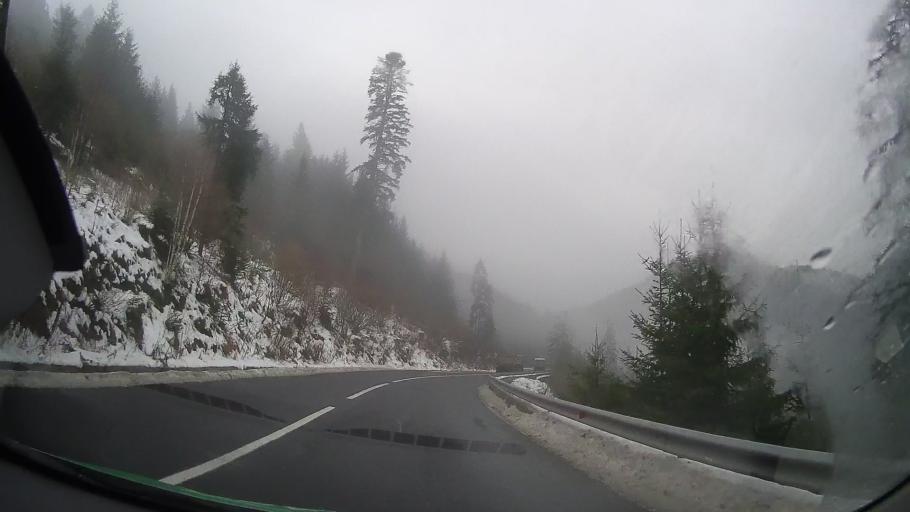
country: RO
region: Harghita
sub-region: Municipiul Gheorgheni
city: Gheorgheni
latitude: 46.7678
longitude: 25.7067
